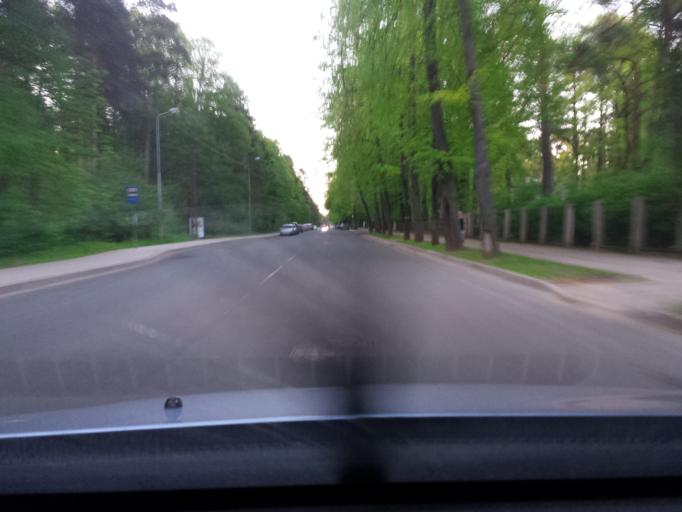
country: LV
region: Riga
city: Jaunciems
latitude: 57.0003
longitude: 24.1484
